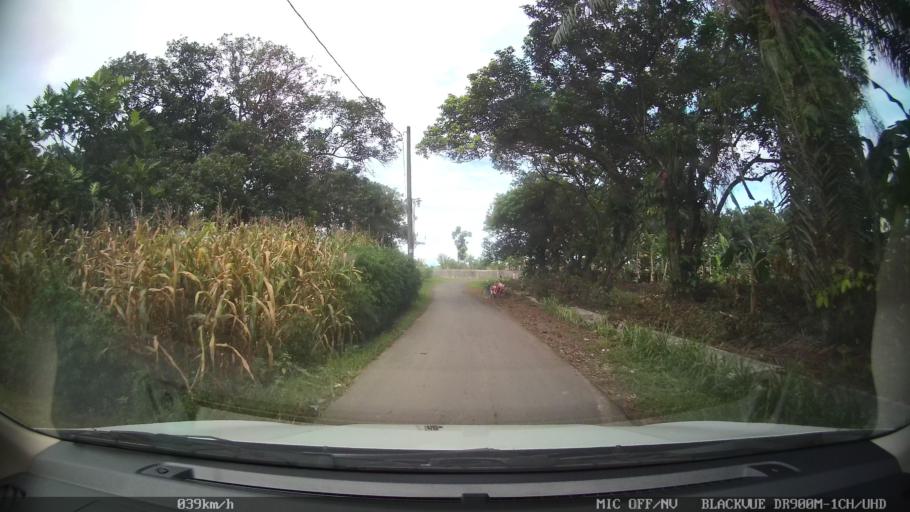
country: ID
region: North Sumatra
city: Sunggal
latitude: 3.5865
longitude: 98.5804
